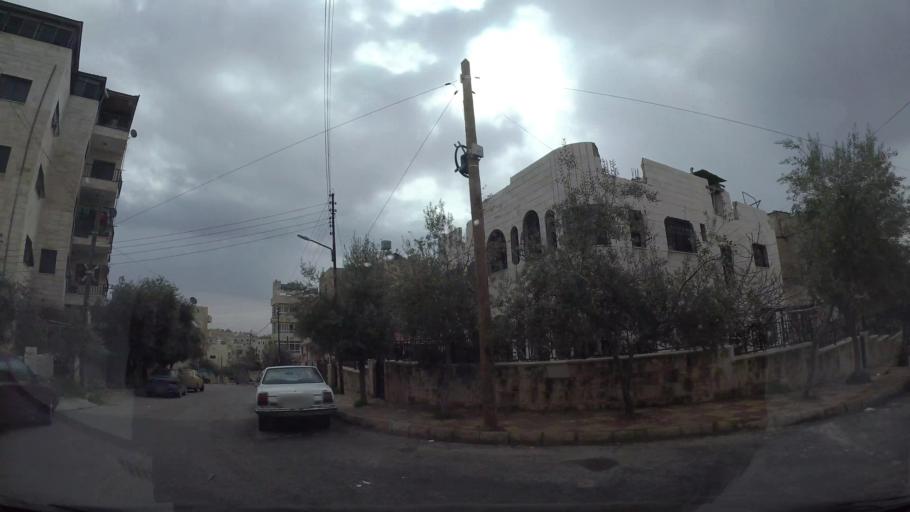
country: JO
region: Amman
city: Amman
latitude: 31.9804
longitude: 35.9317
